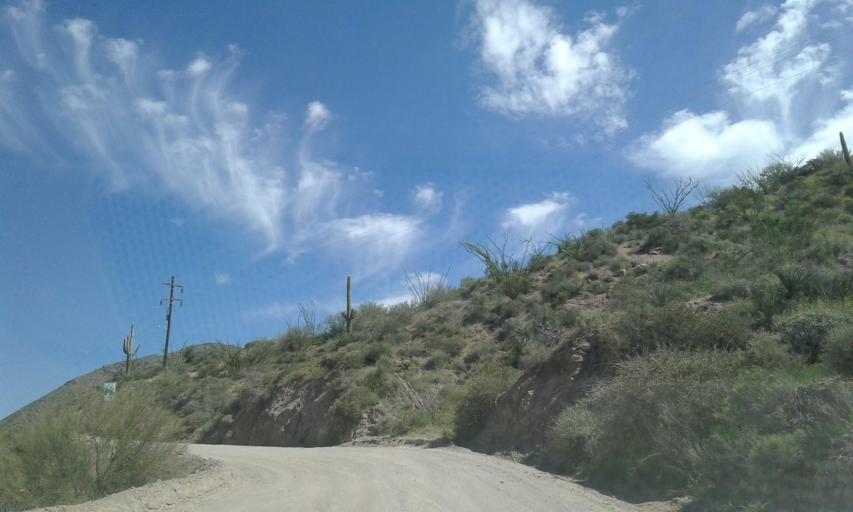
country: US
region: Arizona
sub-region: Gila County
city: Tonto Basin
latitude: 33.5919
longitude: -111.2096
